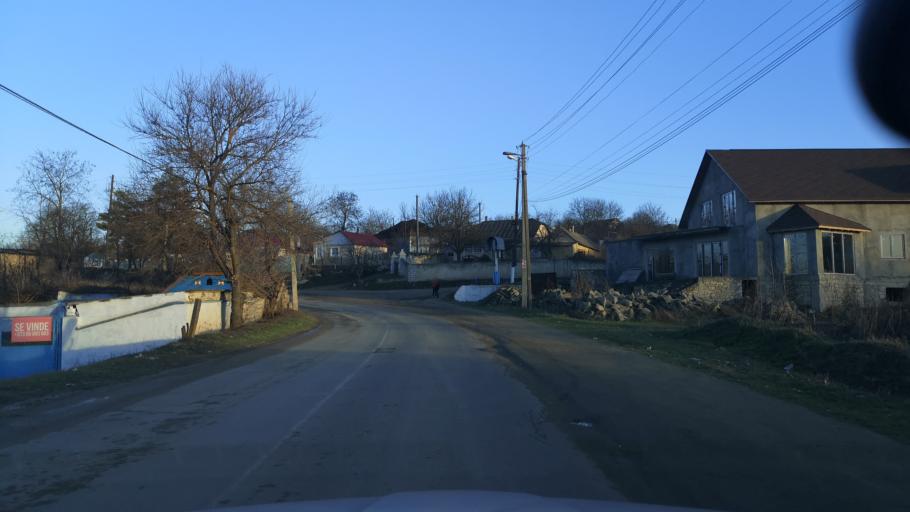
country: MD
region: Orhei
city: Orhei
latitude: 47.3055
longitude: 28.9263
